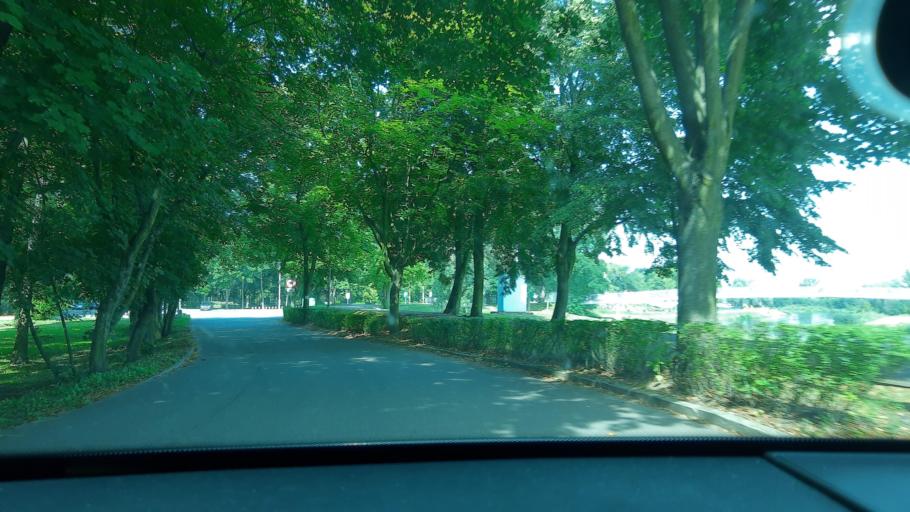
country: PL
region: Lodz Voivodeship
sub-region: Powiat sieradzki
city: Sieradz
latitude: 51.5994
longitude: 18.7422
